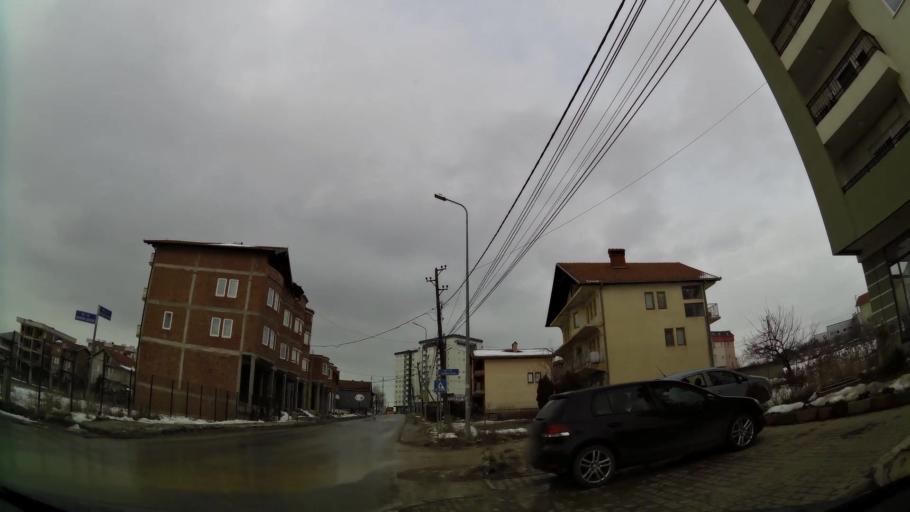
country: XK
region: Pristina
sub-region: Komuna e Prishtines
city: Pristina
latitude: 42.6529
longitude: 21.1920
